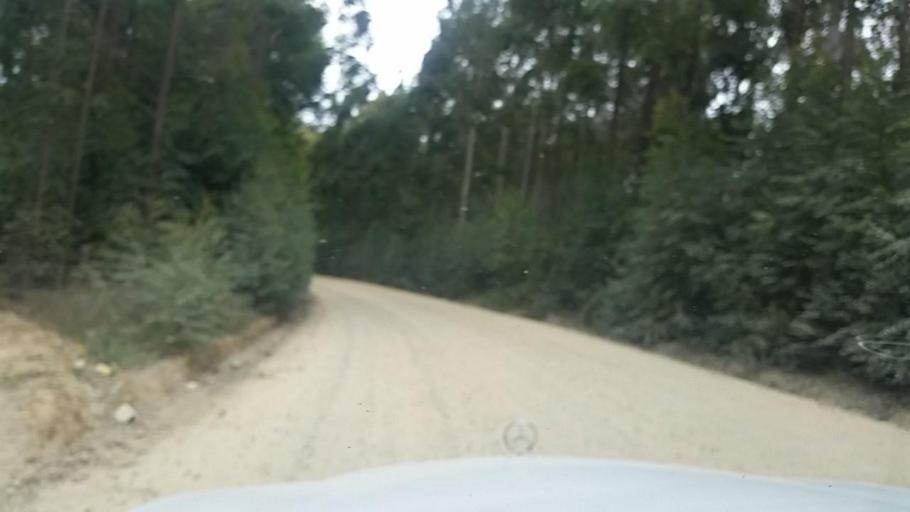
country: ZA
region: Western Cape
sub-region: Eden District Municipality
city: Knysna
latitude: -33.9787
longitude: 23.1366
